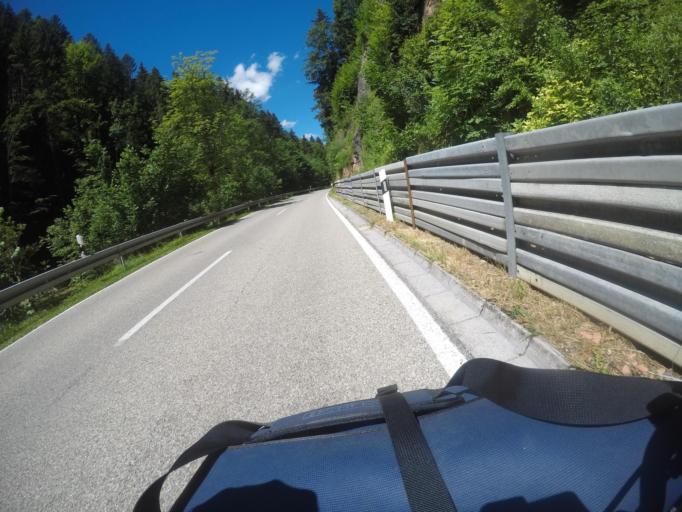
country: DE
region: Bavaria
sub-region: Upper Bavaria
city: Prem
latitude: 47.6534
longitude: 10.7904
